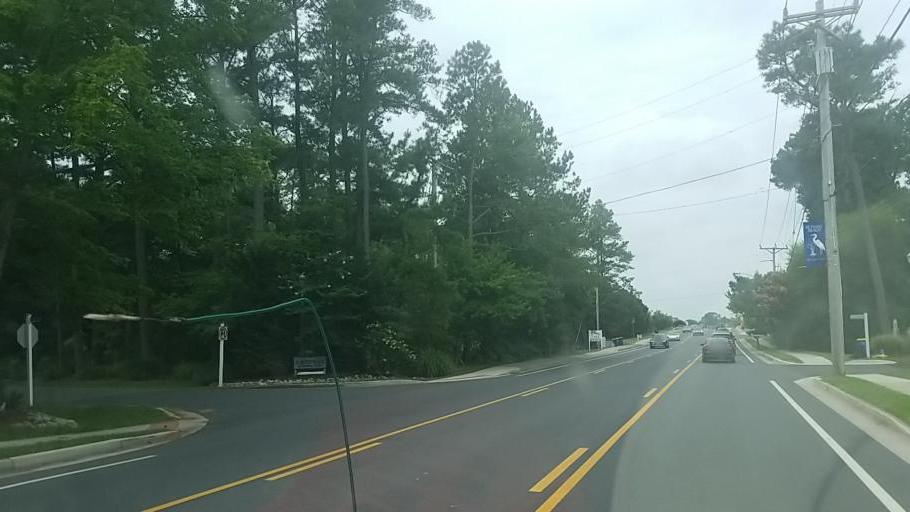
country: US
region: Delaware
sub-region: Sussex County
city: Ocean View
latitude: 38.5420
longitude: -75.0780
